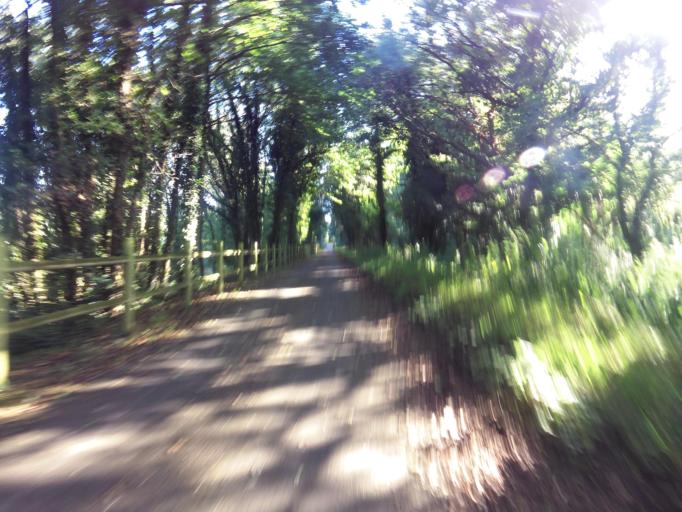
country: FR
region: Brittany
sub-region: Departement du Morbihan
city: Ploermel
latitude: 47.9159
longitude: -2.4288
